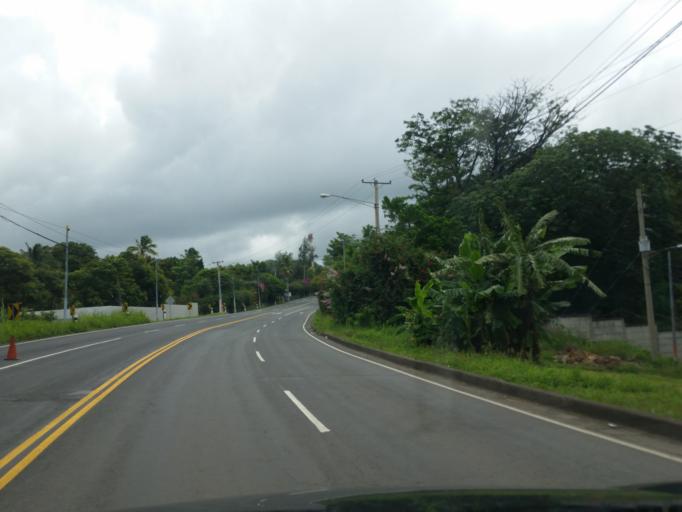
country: NI
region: Managua
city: El Crucero
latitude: 12.0658
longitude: -86.3220
